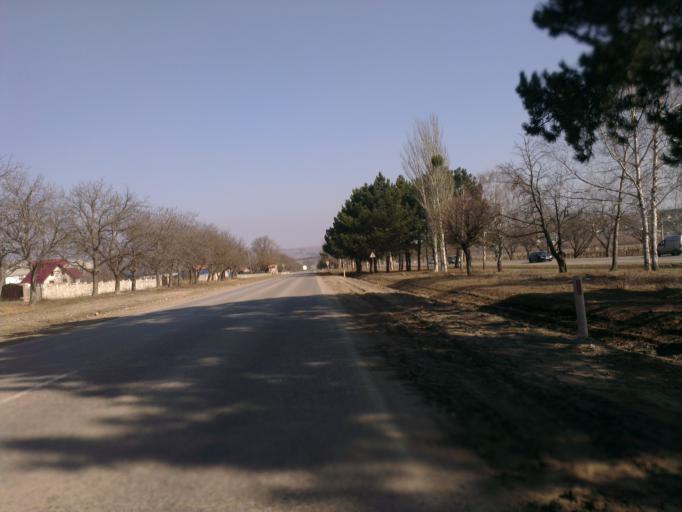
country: MD
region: Chisinau
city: Ciorescu
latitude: 47.1206
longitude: 28.8815
